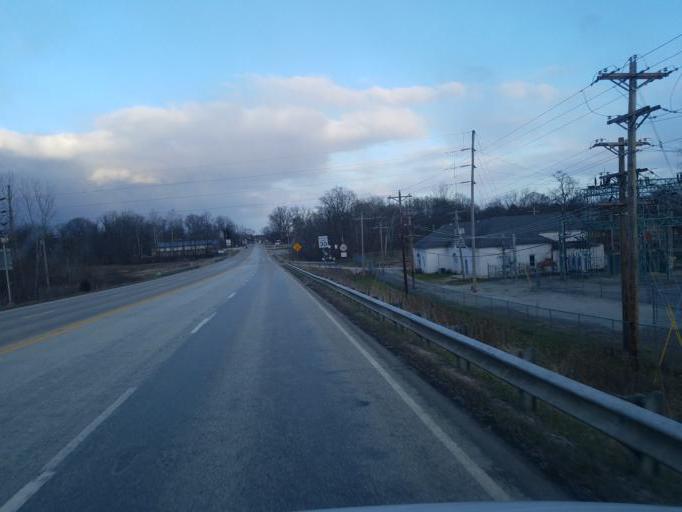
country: US
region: Indiana
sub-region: Henry County
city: Knightstown
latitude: 39.7943
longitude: -85.5380
